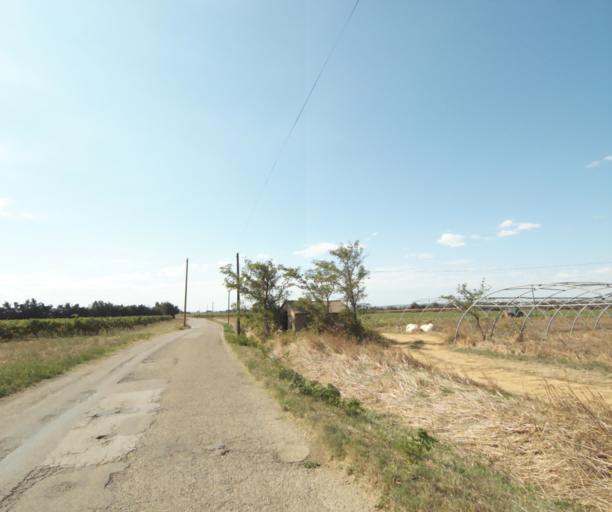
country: FR
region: Languedoc-Roussillon
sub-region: Departement du Gard
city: Manduel
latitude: 43.7994
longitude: 4.4567
